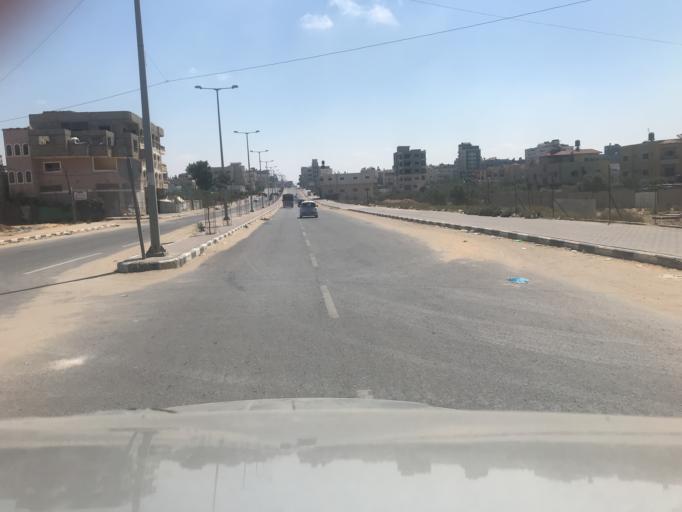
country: PS
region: Gaza Strip
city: Bayt Lahya
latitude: 31.5526
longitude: 34.4692
